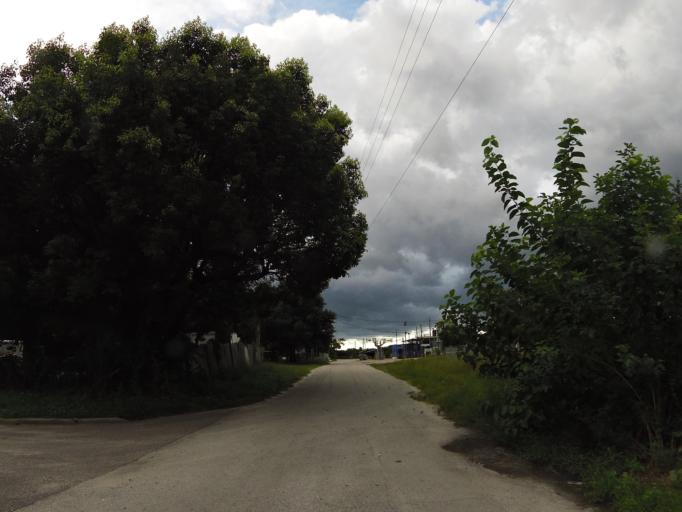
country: US
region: Florida
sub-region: Duval County
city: Jacksonville
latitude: 30.3438
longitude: -81.6314
